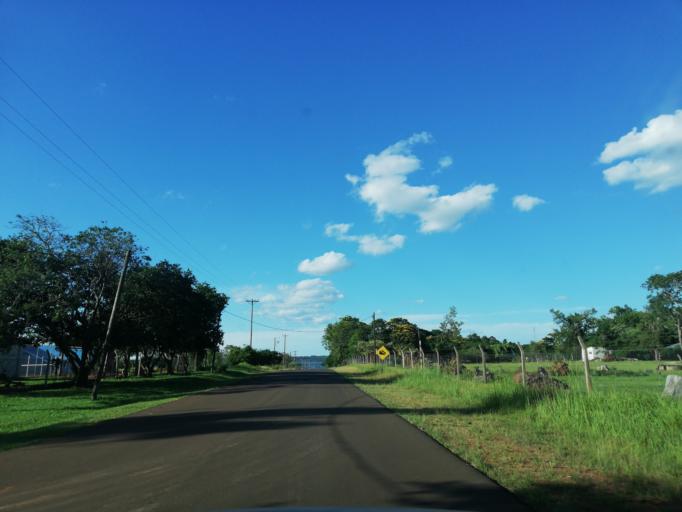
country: AR
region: Misiones
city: Garupa
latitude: -27.4611
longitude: -55.7971
